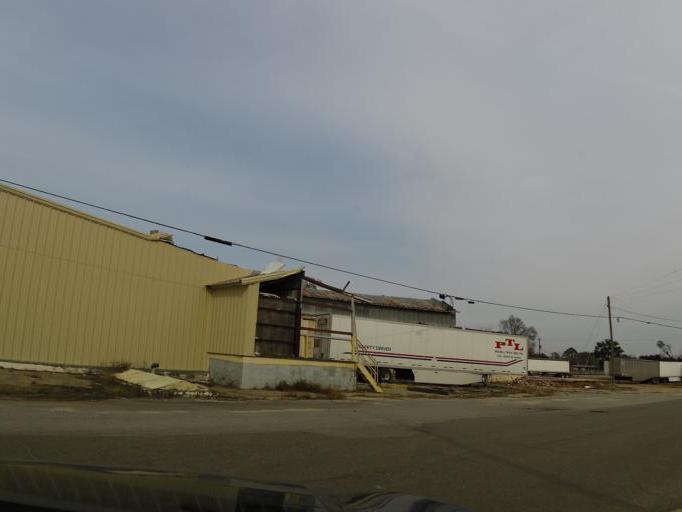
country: US
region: Georgia
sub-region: Seminole County
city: Donalsonville
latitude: 31.0433
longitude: -84.8841
